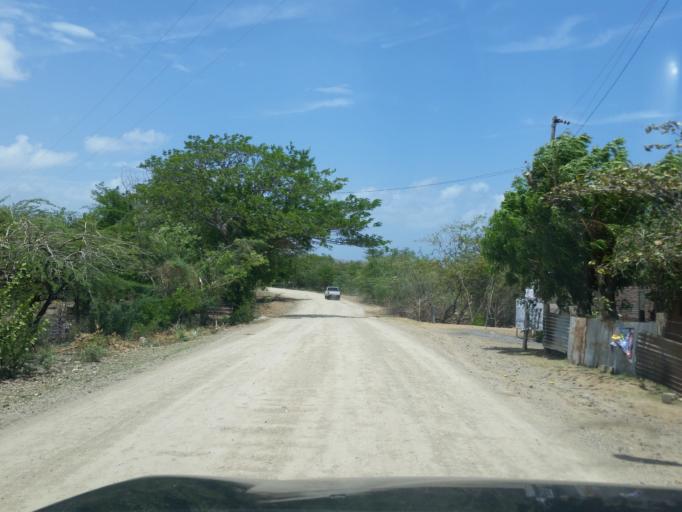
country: NI
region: Rivas
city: Tola
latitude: 11.4727
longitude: -86.1044
